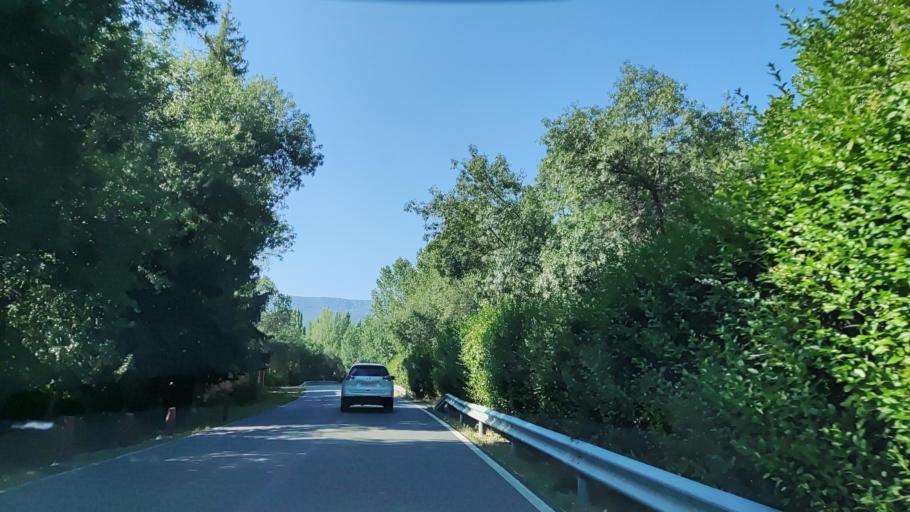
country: ES
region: Madrid
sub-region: Provincia de Madrid
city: Rascafria
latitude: 40.8966
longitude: -3.8802
